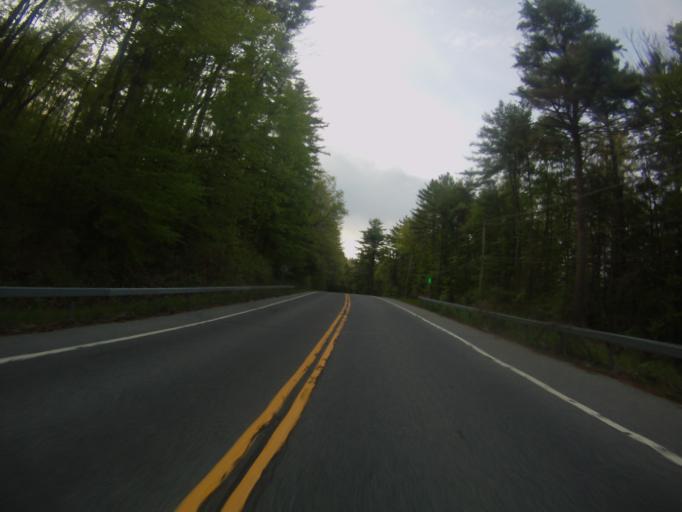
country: US
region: New York
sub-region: Essex County
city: Ticonderoga
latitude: 43.7853
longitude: -73.4872
